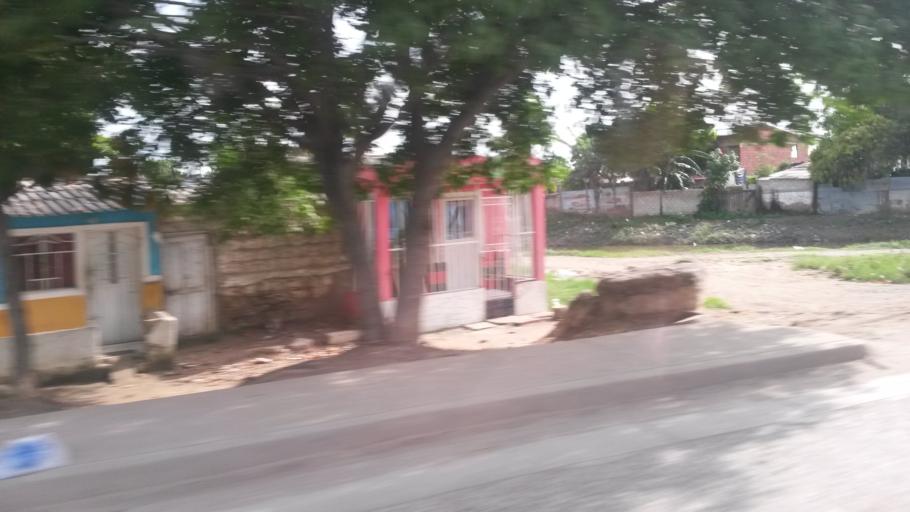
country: CO
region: Bolivar
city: Cartagena
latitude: 10.4031
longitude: -75.4754
